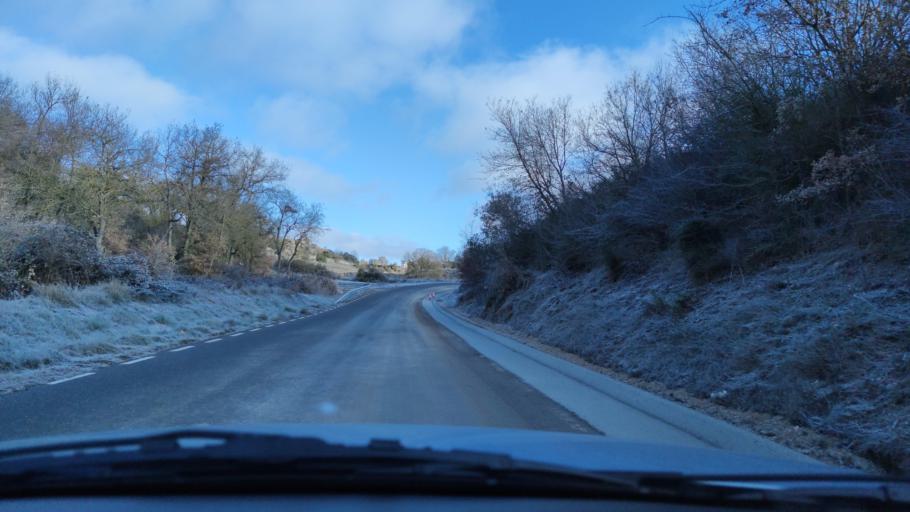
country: ES
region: Catalonia
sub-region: Provincia de Barcelona
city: Pujalt
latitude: 41.7117
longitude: 1.3518
